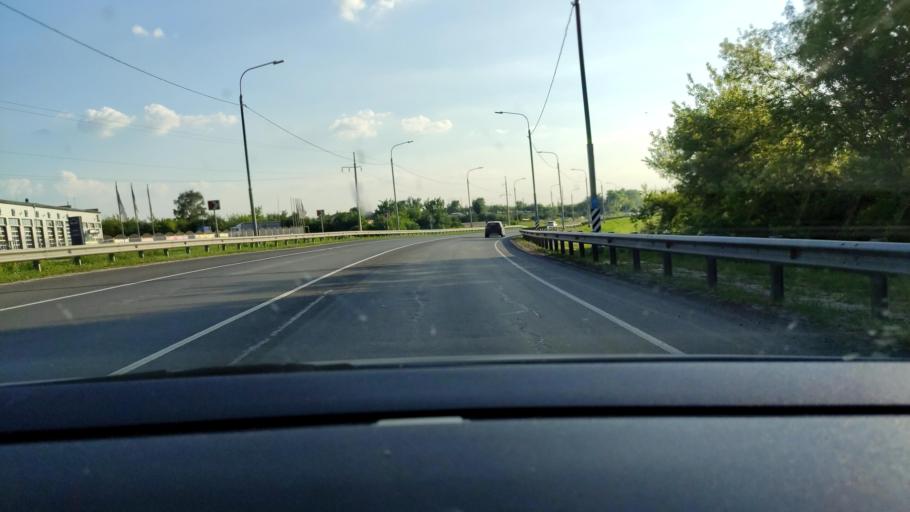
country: RU
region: Voronezj
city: Kashirskoye
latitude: 51.4979
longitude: 39.5569
